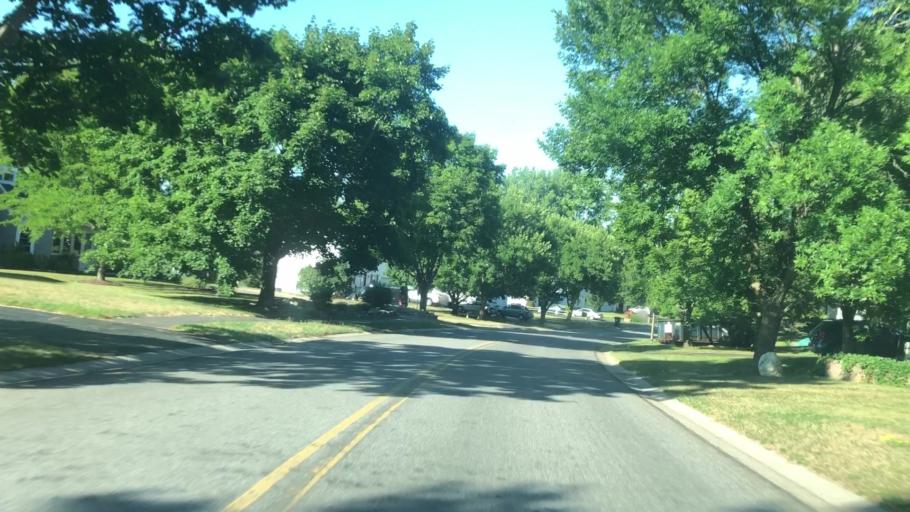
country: US
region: New York
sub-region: Wayne County
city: Macedon
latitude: 43.1274
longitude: -77.2980
